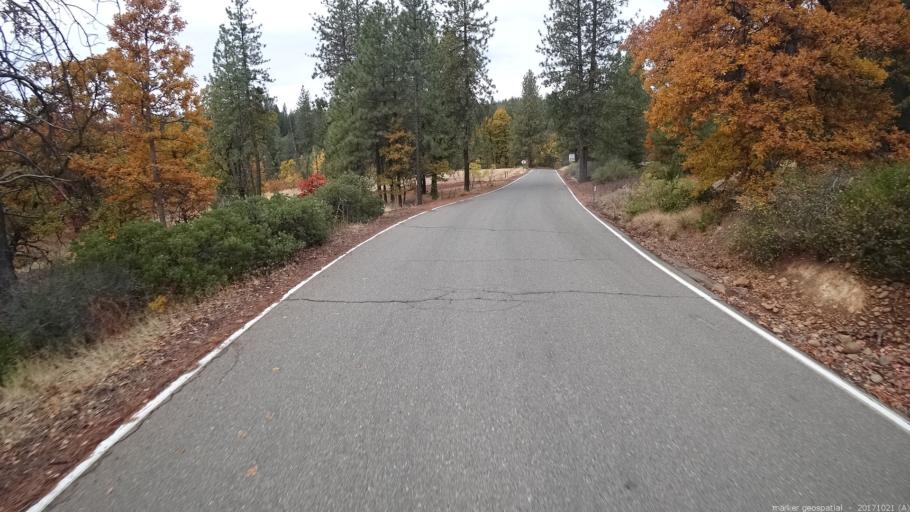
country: US
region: California
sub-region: Shasta County
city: Burney
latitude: 41.0437
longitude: -121.6707
